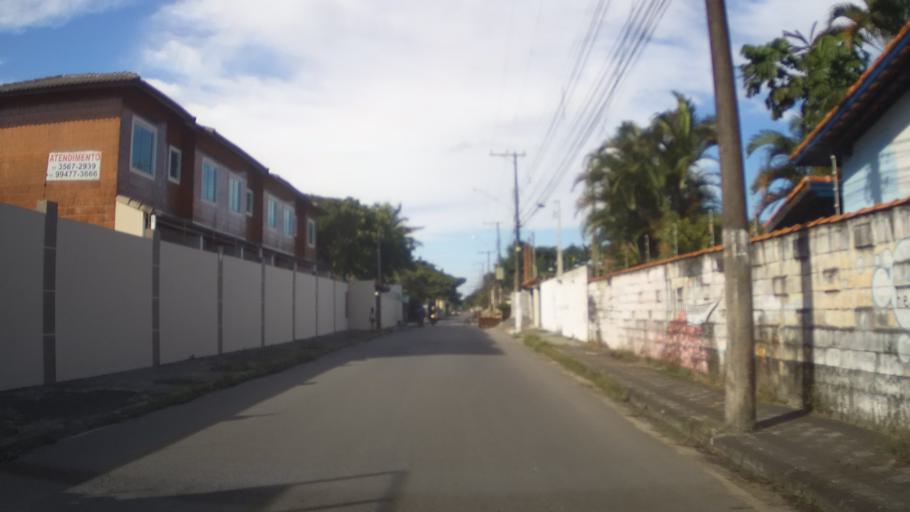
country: BR
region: Sao Paulo
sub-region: Itanhaem
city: Itanhaem
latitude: -24.1677
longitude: -46.7576
